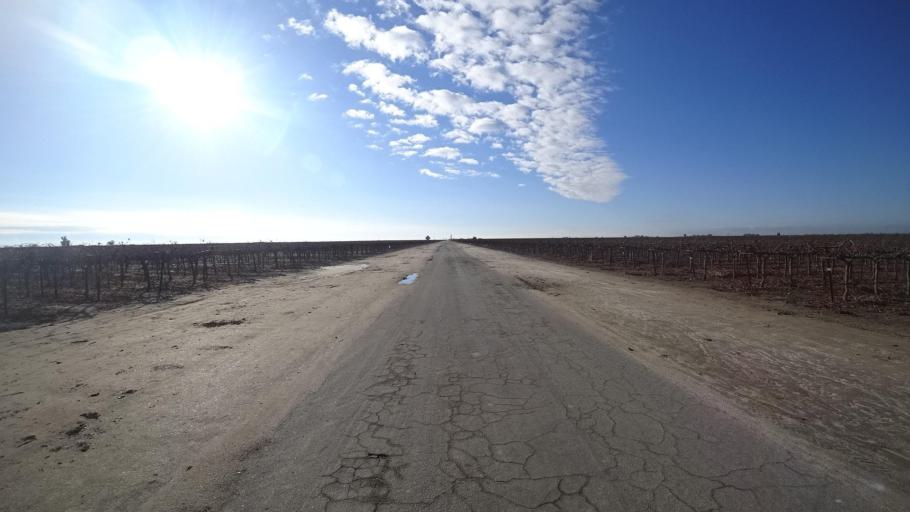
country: US
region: California
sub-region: Kern County
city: Delano
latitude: 35.7318
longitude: -119.3031
